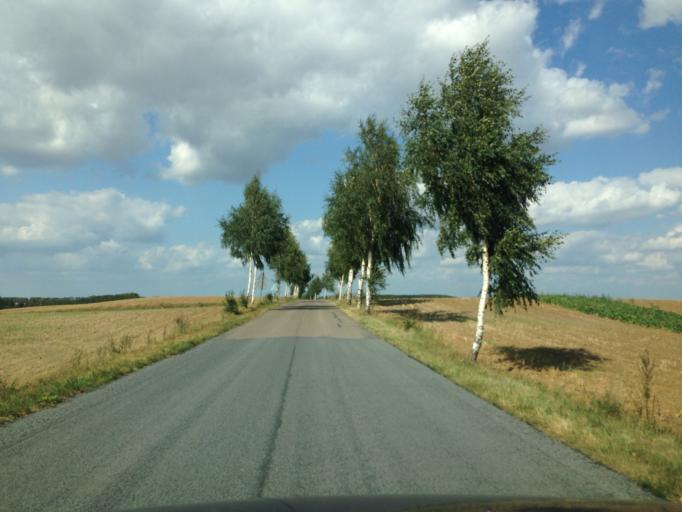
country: PL
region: Kujawsko-Pomorskie
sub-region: Powiat brodnicki
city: Brzozie
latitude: 53.3231
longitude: 19.6644
